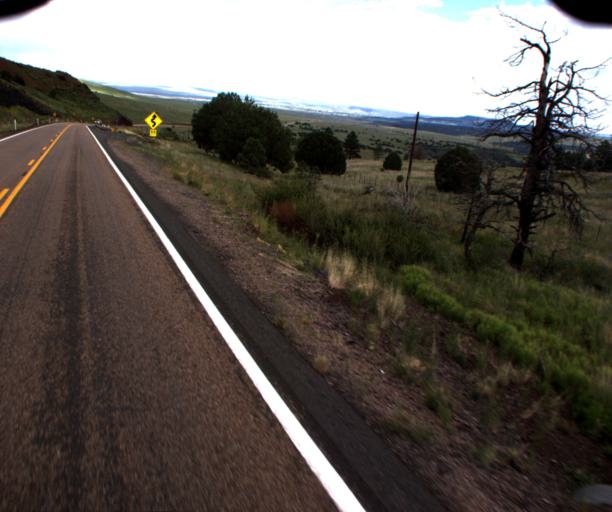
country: US
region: Arizona
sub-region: Apache County
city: Eagar
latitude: 34.0910
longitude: -109.4348
